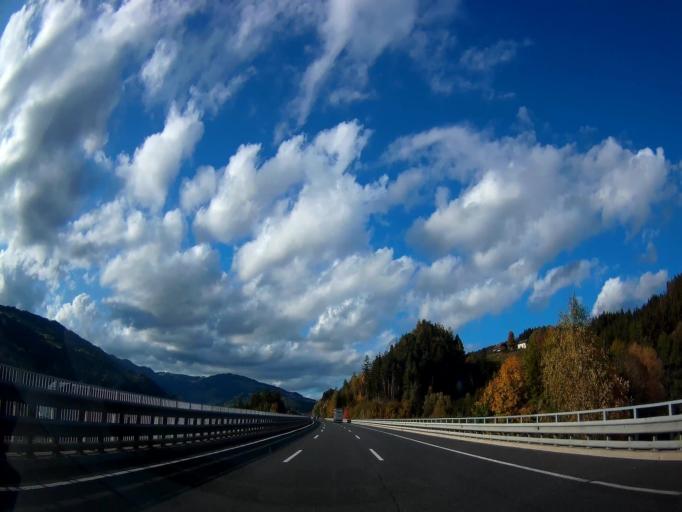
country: AT
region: Carinthia
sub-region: Politischer Bezirk Wolfsberg
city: Wolfsberg
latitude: 46.8855
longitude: 14.8284
